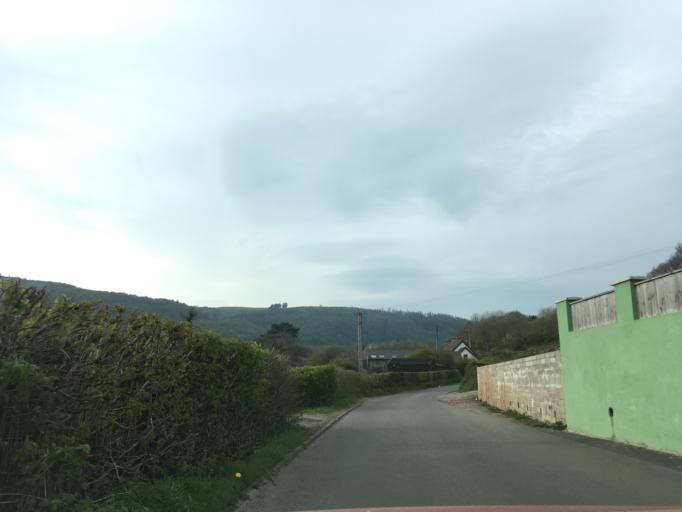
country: GB
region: Wales
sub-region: Caerphilly County Borough
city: Llanbradach
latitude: 51.5960
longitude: -3.2227
